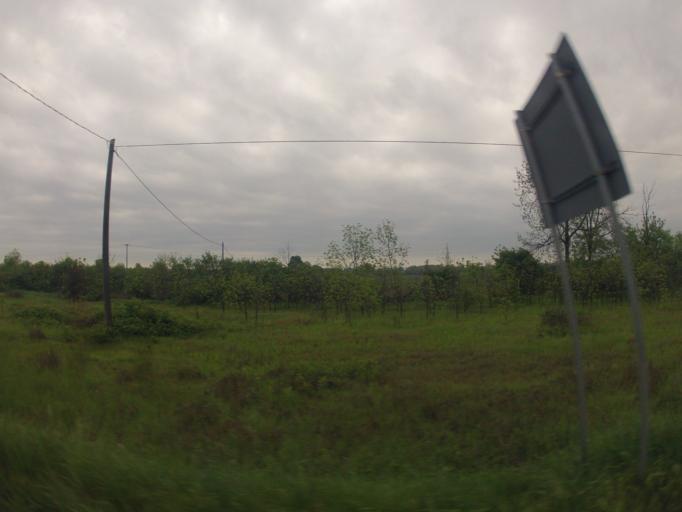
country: IT
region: Piedmont
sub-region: Provincia di Torino
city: Carignano
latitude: 44.8905
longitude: 7.6688
